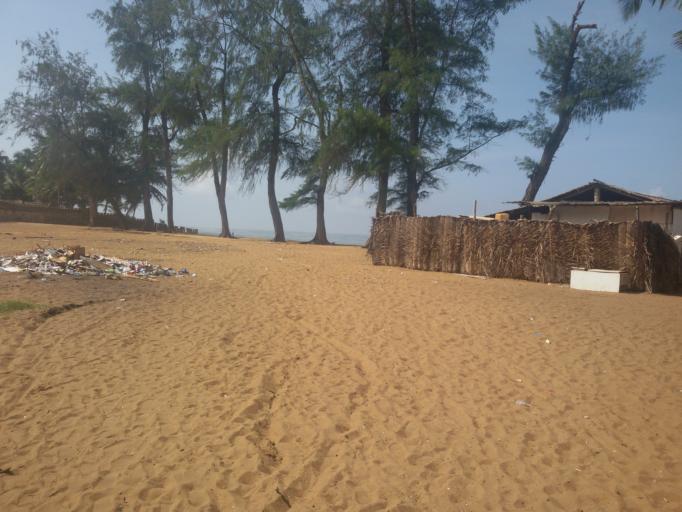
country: CI
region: Sud-Comoe
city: Grand-Bassam
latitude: 5.1942
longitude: -3.7339
